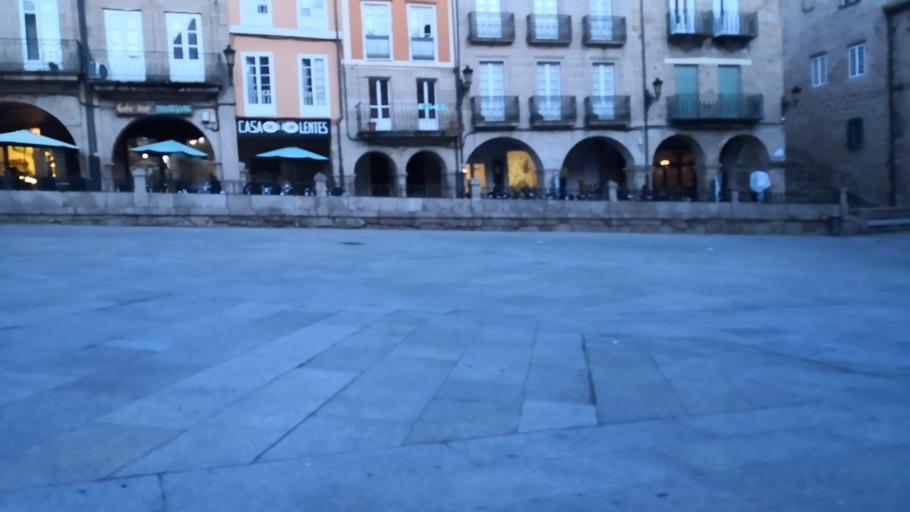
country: ES
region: Galicia
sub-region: Provincia de Ourense
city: Ourense
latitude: 42.3359
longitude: -7.8641
